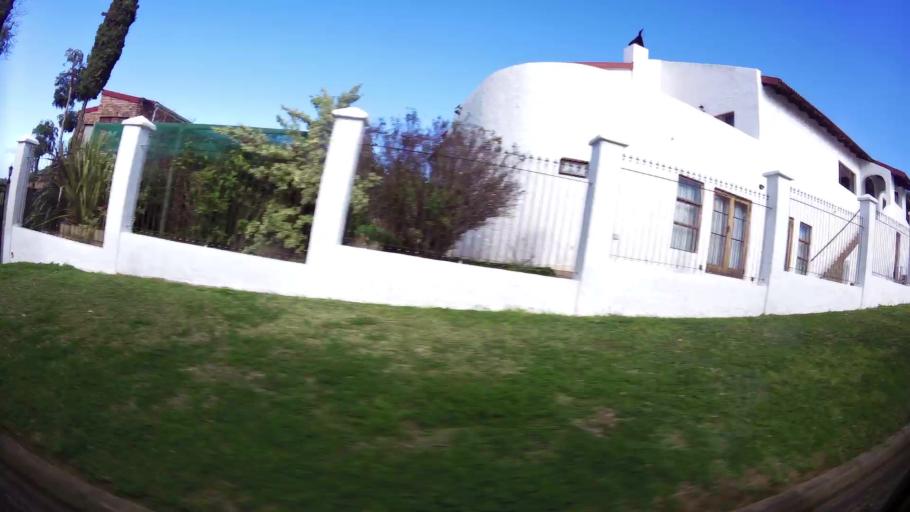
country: ZA
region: Western Cape
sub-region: Eden District Municipality
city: George
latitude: -33.9603
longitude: 22.4968
